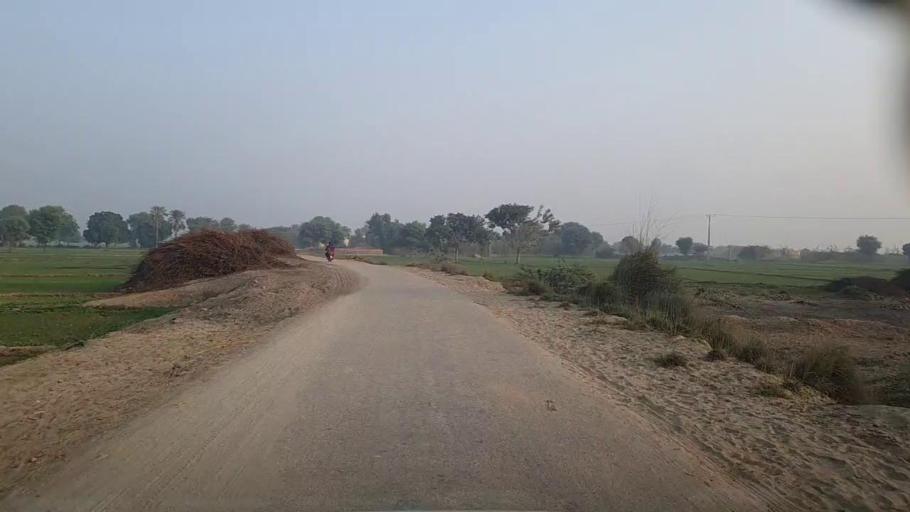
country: PK
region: Sindh
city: Bozdar
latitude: 27.0836
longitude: 68.5650
